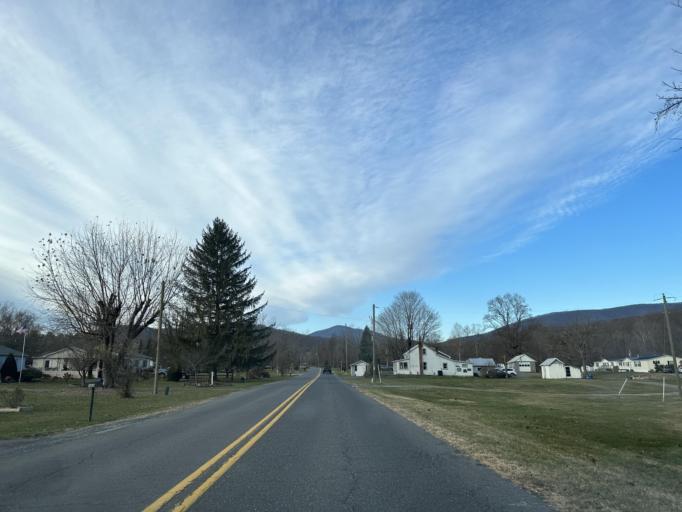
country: US
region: Virginia
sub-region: City of Staunton
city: Staunton
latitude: 38.2158
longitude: -79.2131
